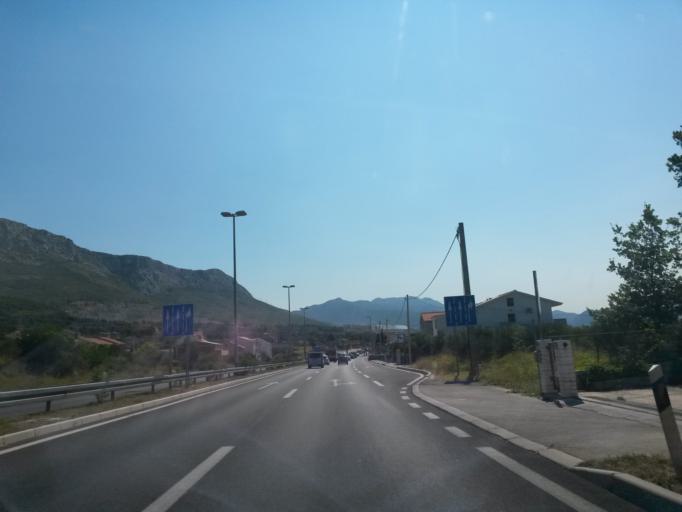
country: HR
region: Splitsko-Dalmatinska
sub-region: Grad Split
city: Split
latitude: 43.5510
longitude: 16.4254
